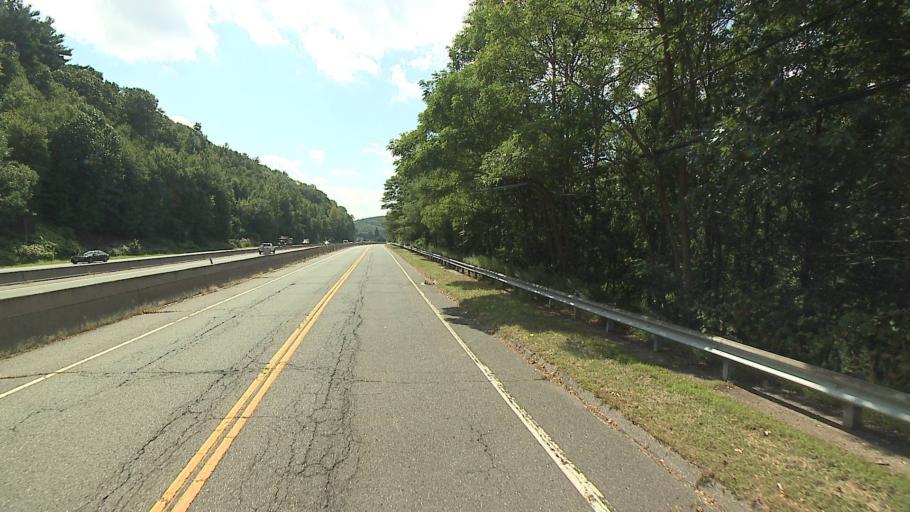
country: US
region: Connecticut
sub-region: New Haven County
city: Seymour
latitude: 41.4196
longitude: -73.0699
